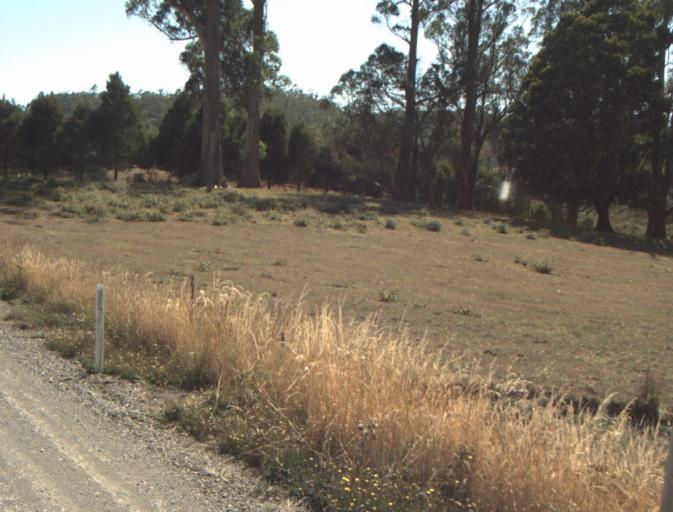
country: AU
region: Tasmania
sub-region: Launceston
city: Mayfield
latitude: -41.2299
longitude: 147.2357
